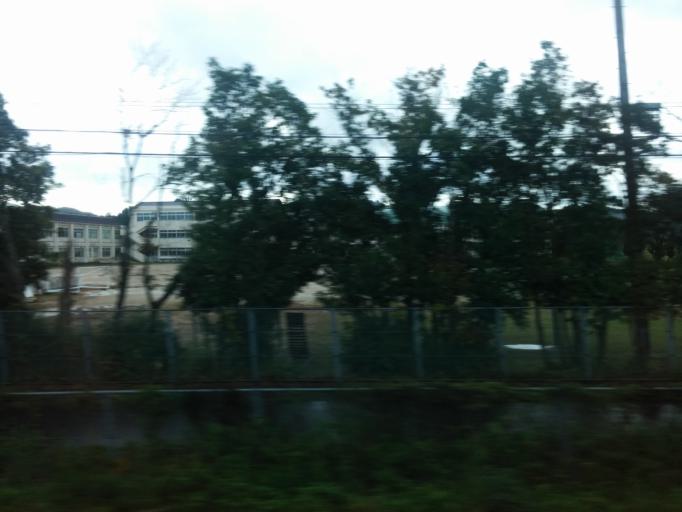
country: JP
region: Shiga Prefecture
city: Omihachiman
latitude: 35.0908
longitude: 136.0570
